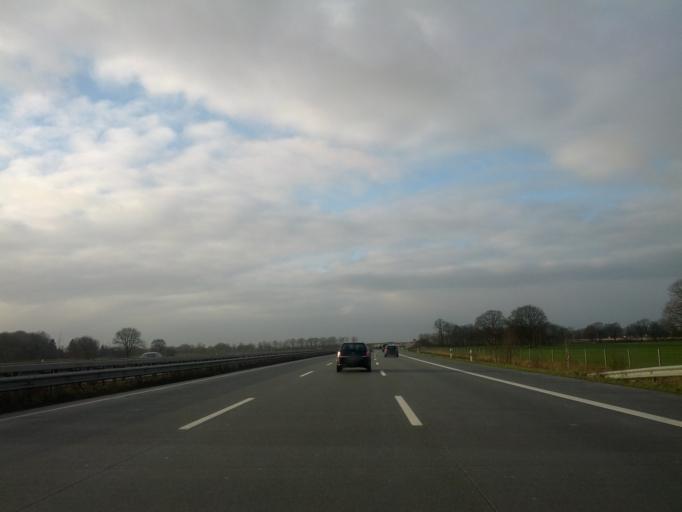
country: DE
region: Lower Saxony
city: Elsdorf
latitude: 53.2376
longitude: 9.3750
